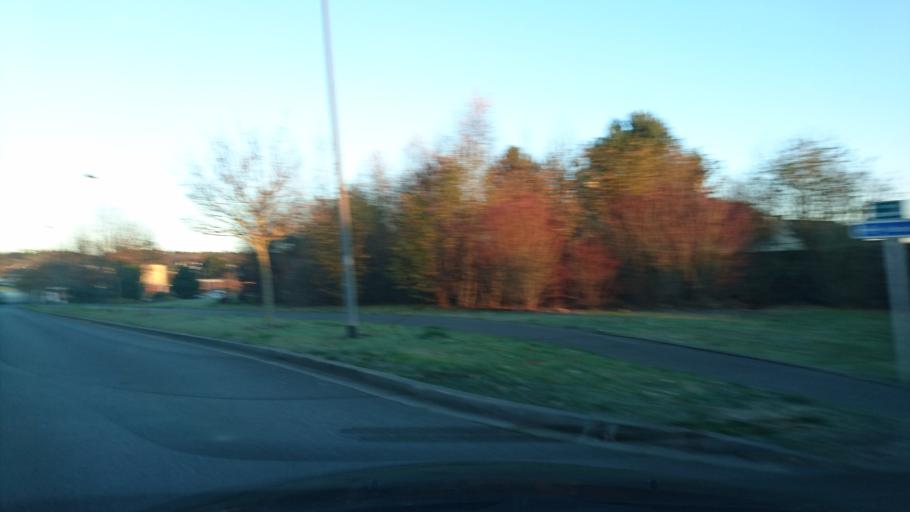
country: FR
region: Brittany
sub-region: Departement des Cotes-d'Armor
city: Pledran
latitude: 48.4463
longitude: -2.7424
